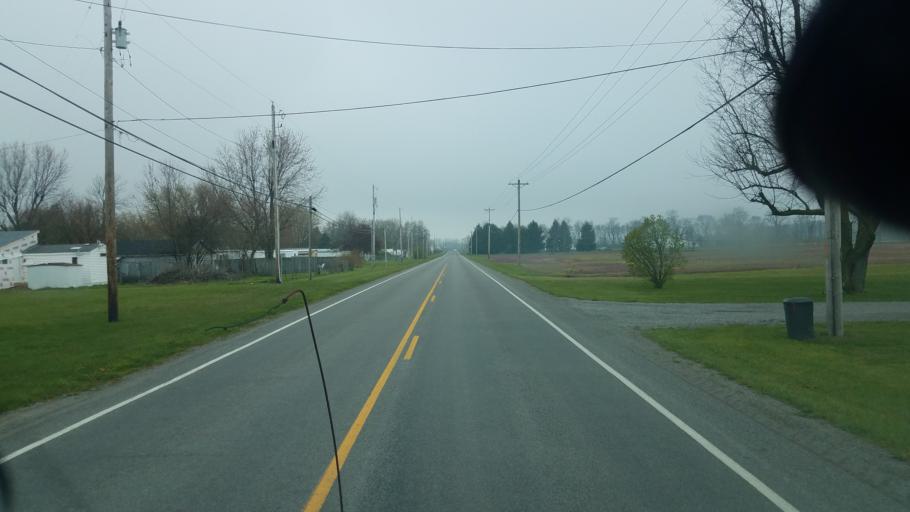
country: US
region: Ohio
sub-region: Logan County
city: Bellefontaine
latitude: 40.4015
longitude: -83.7981
